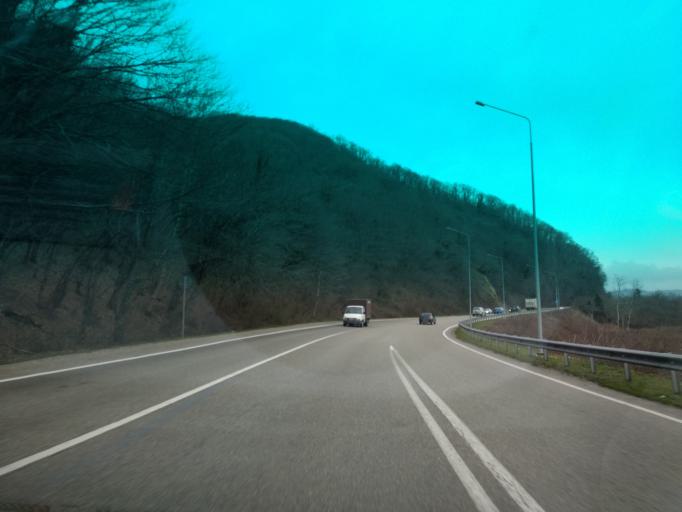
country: RU
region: Krasnodarskiy
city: Ol'ginka
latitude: 44.2179
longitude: 38.8941
